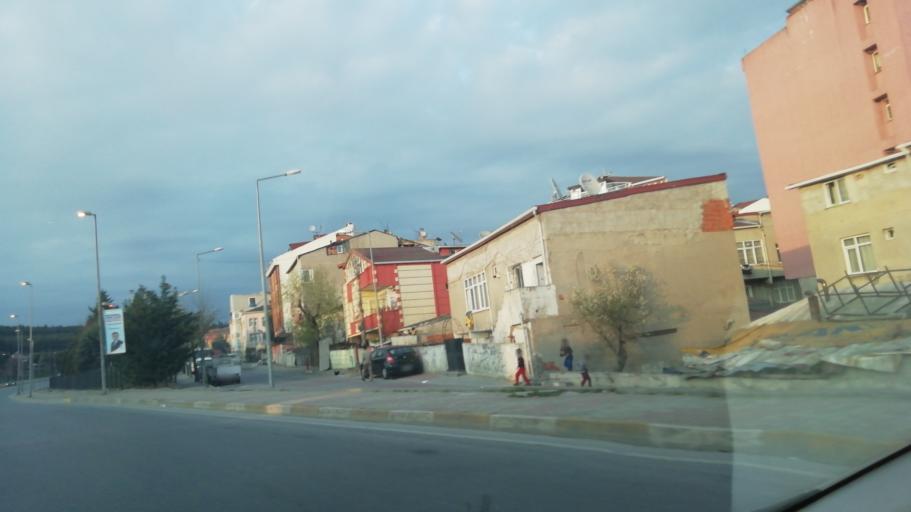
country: TR
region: Istanbul
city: Mahmutbey
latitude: 41.0203
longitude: 28.7819
